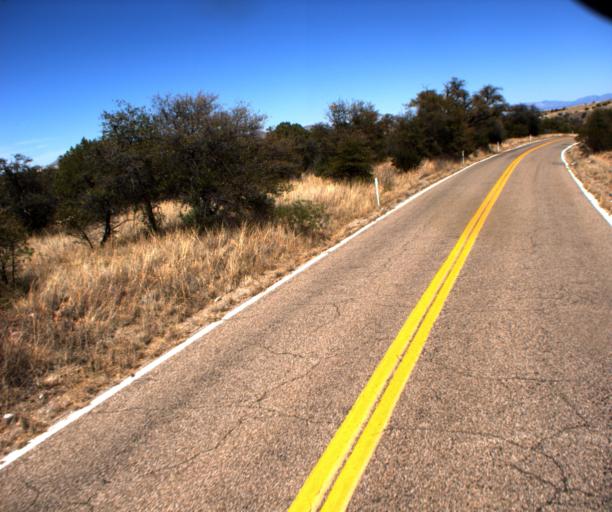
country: US
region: Arizona
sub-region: Cochise County
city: Huachuca City
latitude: 31.5546
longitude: -110.5345
